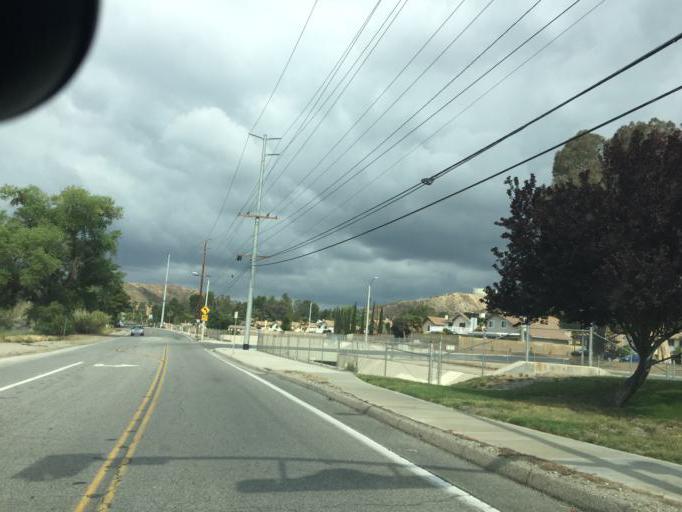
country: US
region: California
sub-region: Los Angeles County
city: Santa Clarita
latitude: 34.4596
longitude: -118.4918
